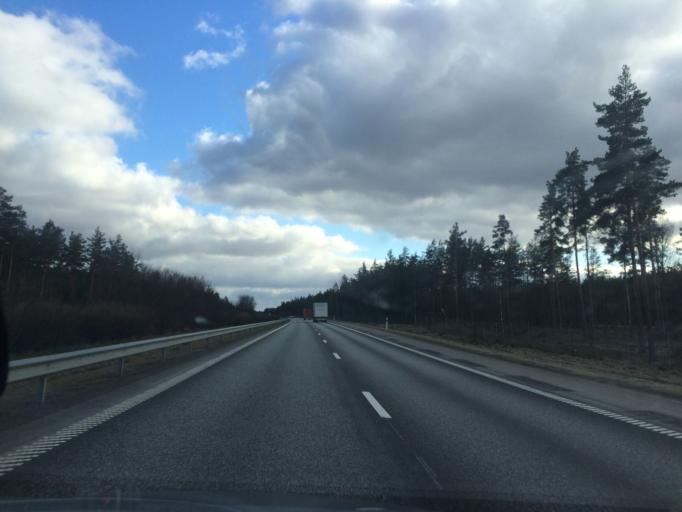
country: SE
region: Joenkoeping
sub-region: Vaggeryds Kommun
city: Skillingaryd
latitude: 57.3783
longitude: 14.1003
